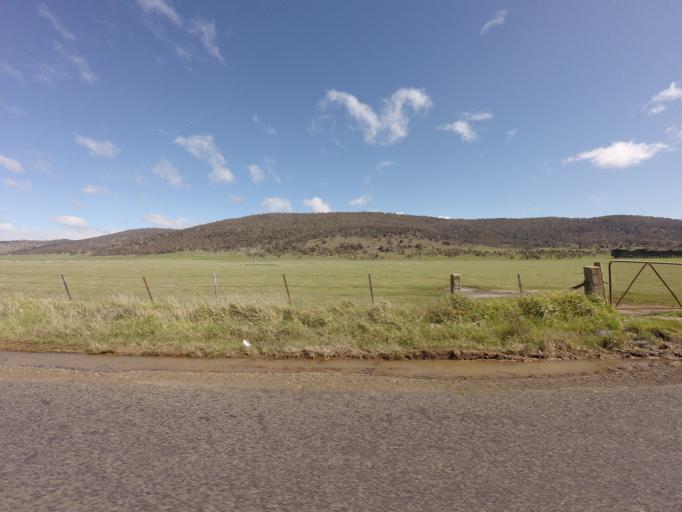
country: AU
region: Tasmania
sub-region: Northern Midlands
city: Evandale
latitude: -41.9699
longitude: 147.4427
